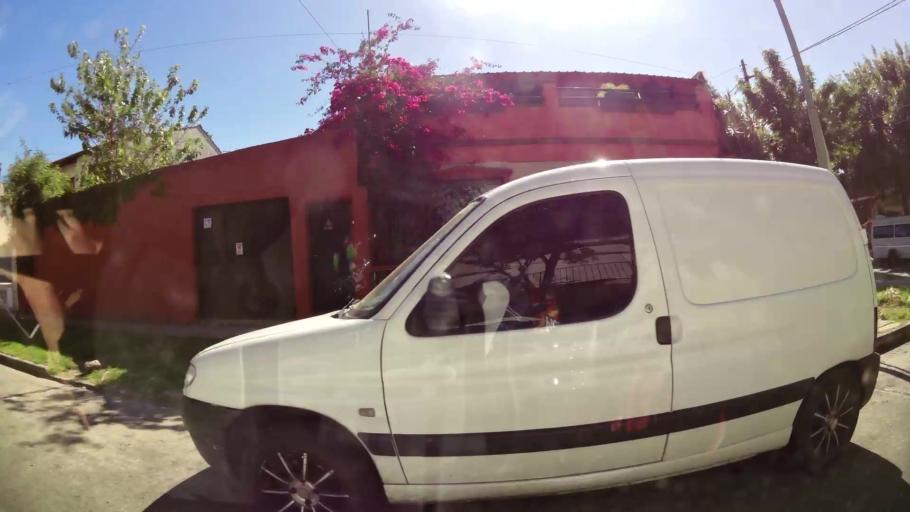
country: AR
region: Buenos Aires
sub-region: Partido de General San Martin
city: General San Martin
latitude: -34.5404
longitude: -58.5110
